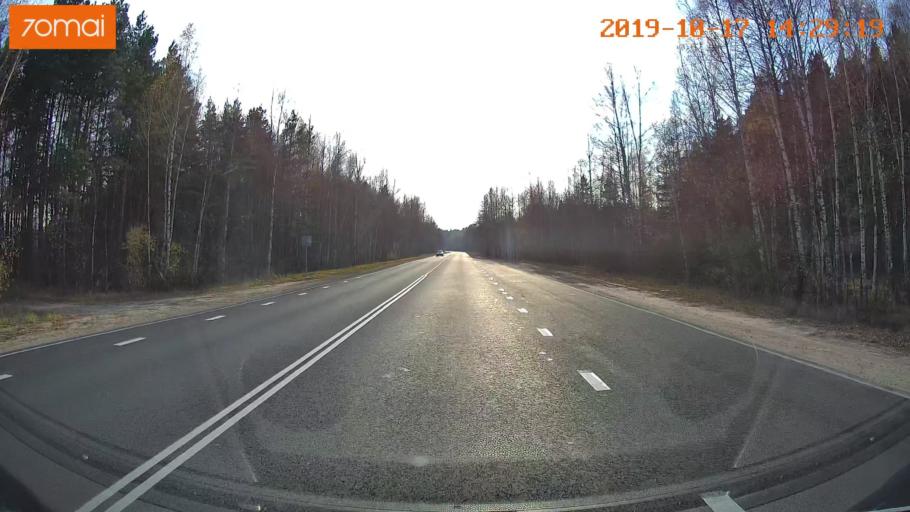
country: RU
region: Rjazan
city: Solotcha
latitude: 54.9621
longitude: 39.9428
